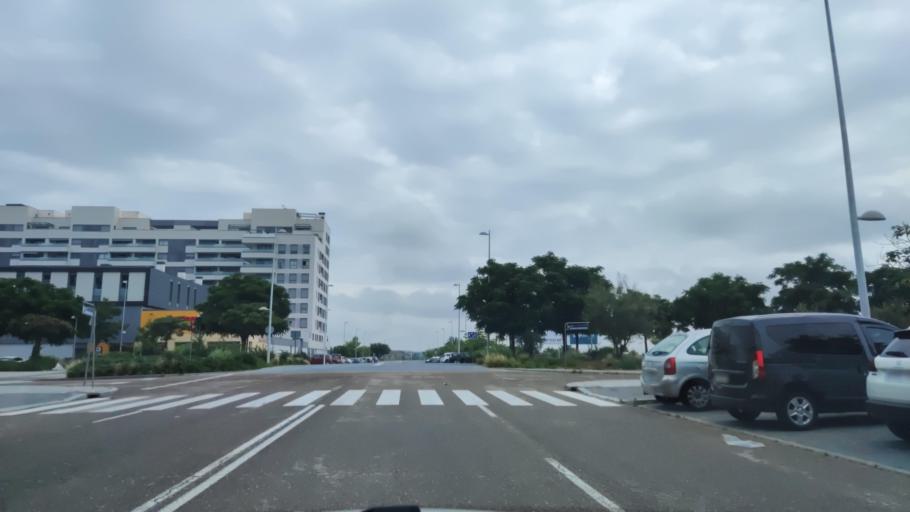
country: ES
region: Madrid
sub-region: Provincia de Madrid
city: Barajas de Madrid
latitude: 40.4908
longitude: -3.6066
